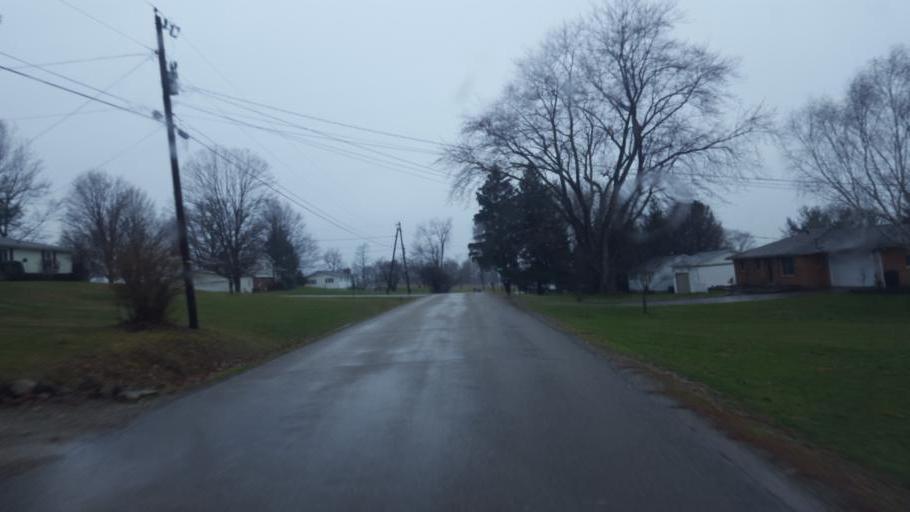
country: US
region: Ohio
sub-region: Knox County
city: Mount Vernon
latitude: 40.4379
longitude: -82.4913
